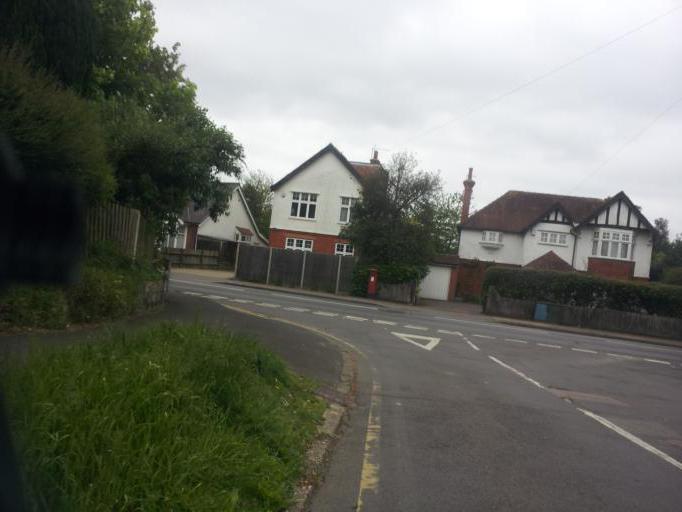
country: GB
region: England
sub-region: Kent
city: Maidstone
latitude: 51.2469
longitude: 0.5253
